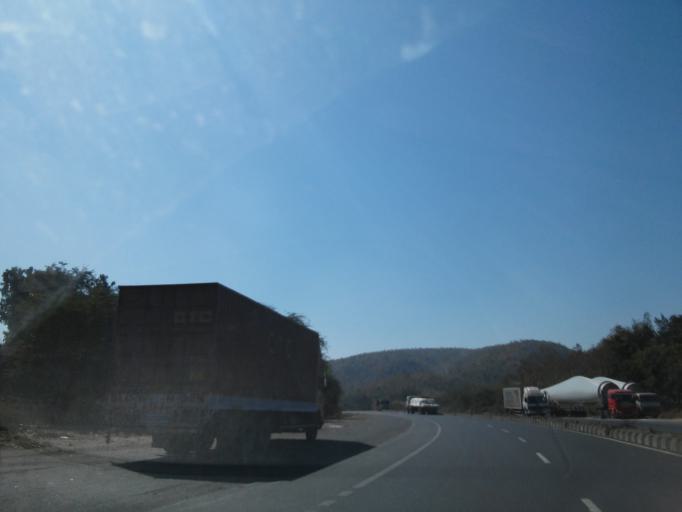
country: IN
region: Gujarat
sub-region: Sabar Kantha
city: Meghraj
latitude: 23.7145
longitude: 73.3920
